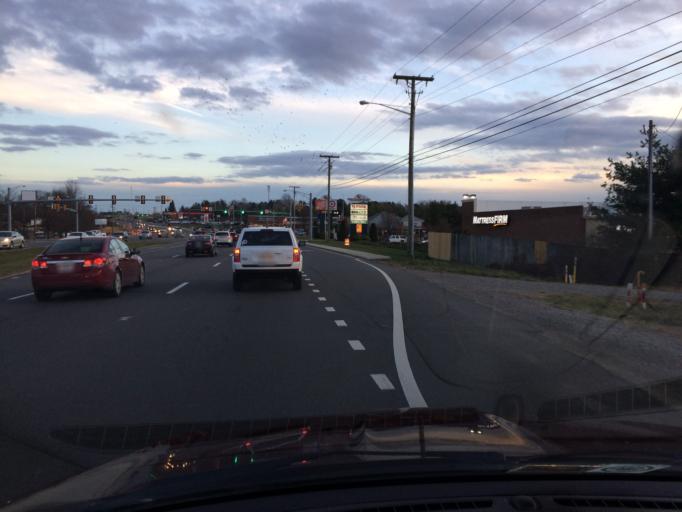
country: US
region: Virginia
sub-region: Montgomery County
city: Merrimac
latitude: 37.1612
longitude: -80.4226
